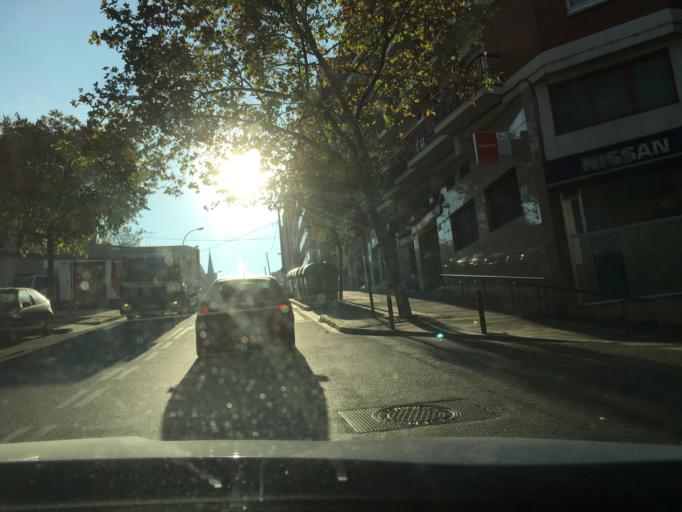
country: ES
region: Catalonia
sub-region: Provincia de Barcelona
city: Santa Coloma de Gramenet
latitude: 41.4553
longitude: 2.2098
